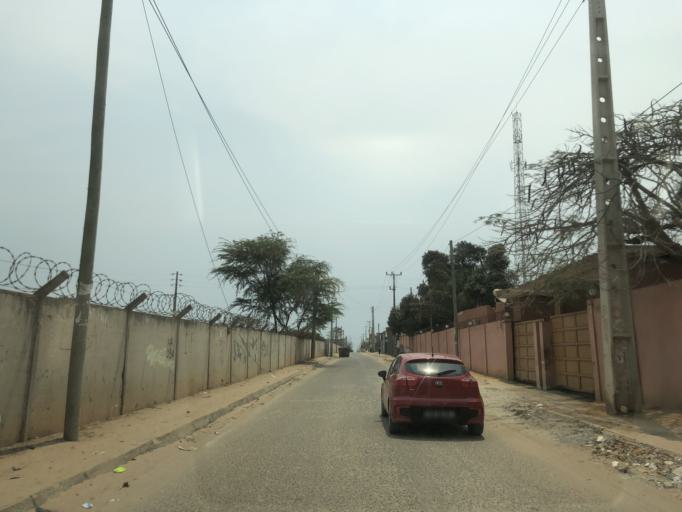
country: AO
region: Luanda
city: Luanda
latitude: -8.8891
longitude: 13.1959
